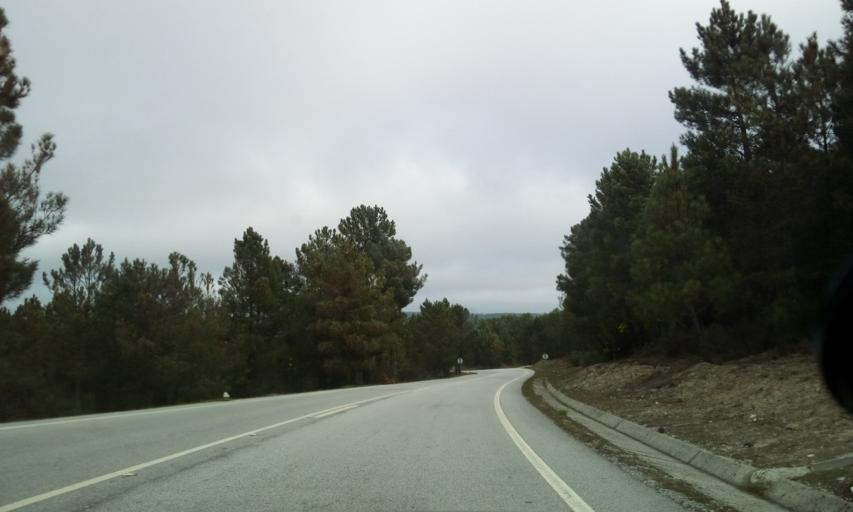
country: PT
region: Guarda
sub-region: Fornos de Algodres
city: Fornos de Algodres
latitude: 40.7113
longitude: -7.4864
